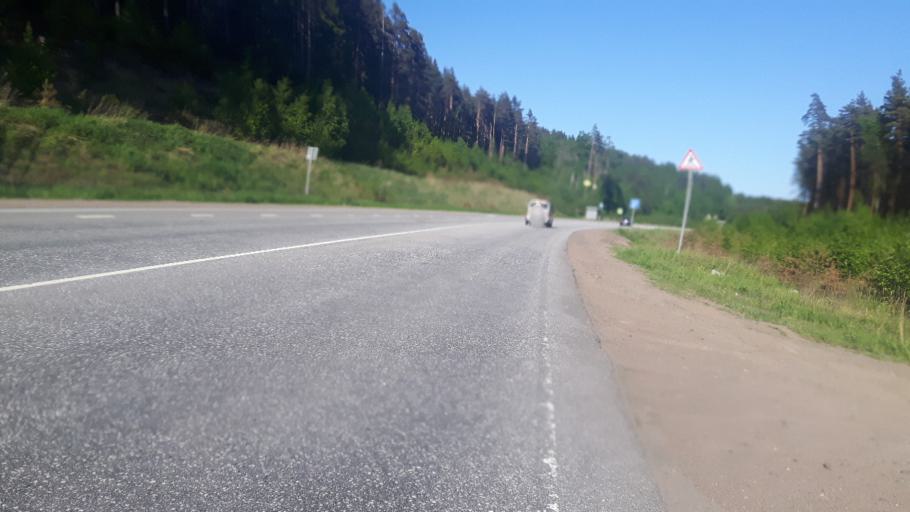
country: RU
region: Leningrad
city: Sosnovyy Bor
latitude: 60.1676
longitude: 29.1714
